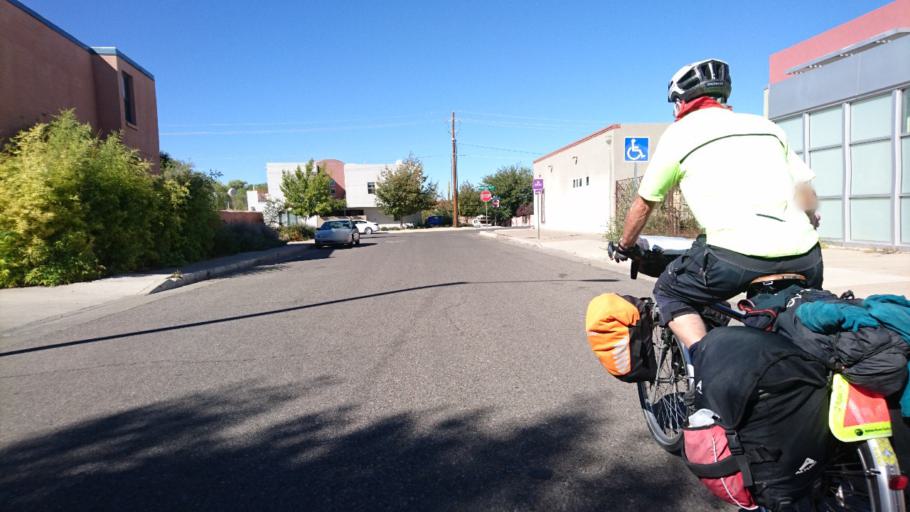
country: US
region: New Mexico
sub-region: Bernalillo County
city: Albuquerque
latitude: 35.0783
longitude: -106.5993
